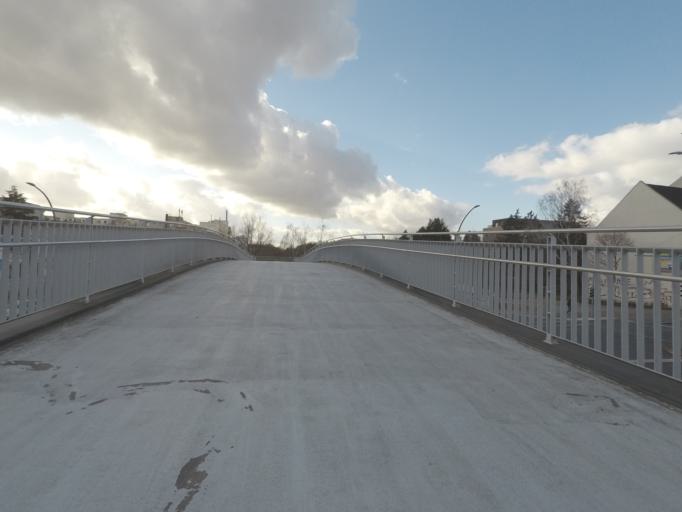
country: DE
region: Berlin
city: Britz
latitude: 52.4622
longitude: 13.4349
